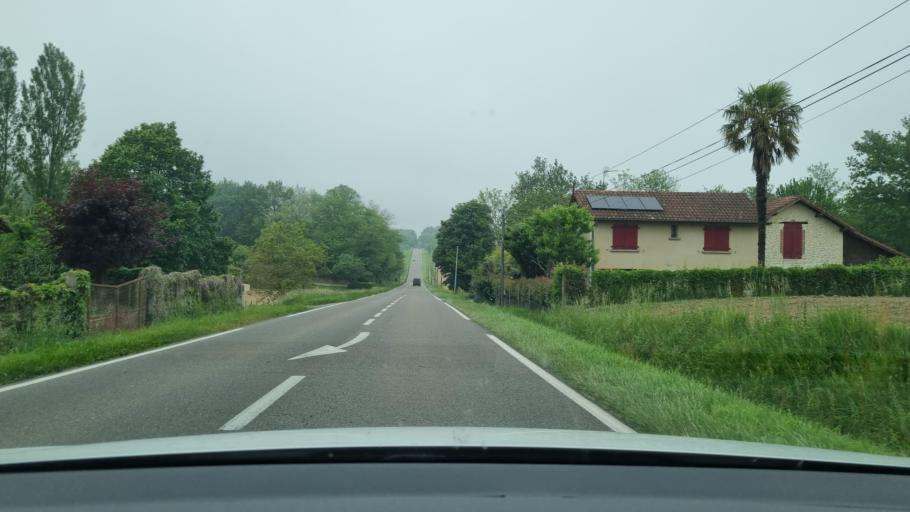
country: FR
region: Aquitaine
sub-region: Departement des Landes
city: Saint-Sever
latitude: 43.7188
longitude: -0.5773
